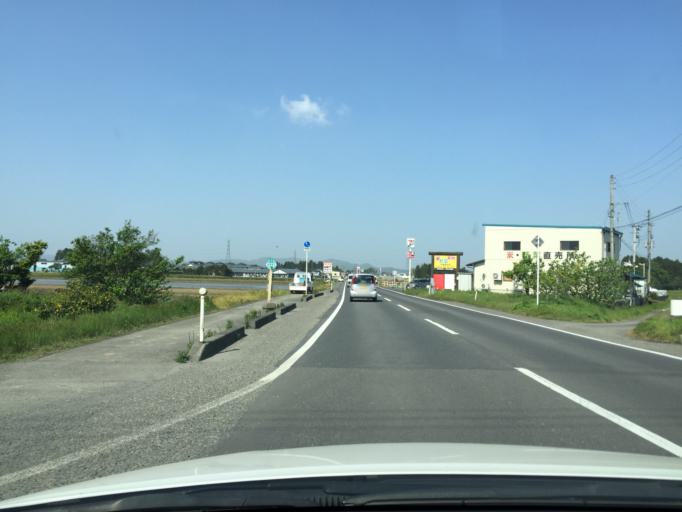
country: JP
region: Niigata
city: Gosen
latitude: 37.7486
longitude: 139.2104
